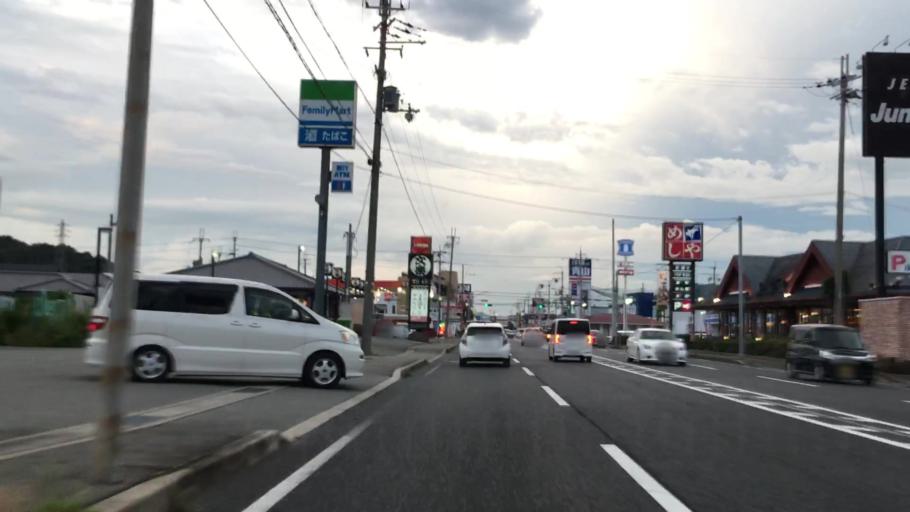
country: JP
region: Hyogo
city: Himeji
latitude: 34.8642
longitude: 134.7256
